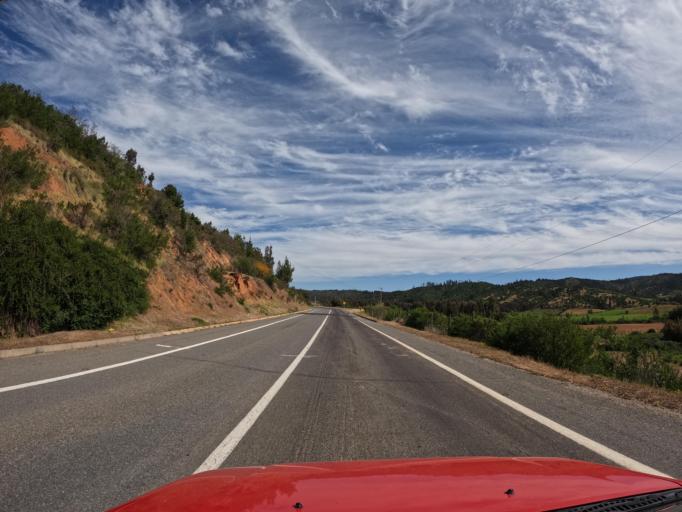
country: CL
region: Maule
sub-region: Provincia de Talca
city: Talca
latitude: -35.1368
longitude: -71.9638
